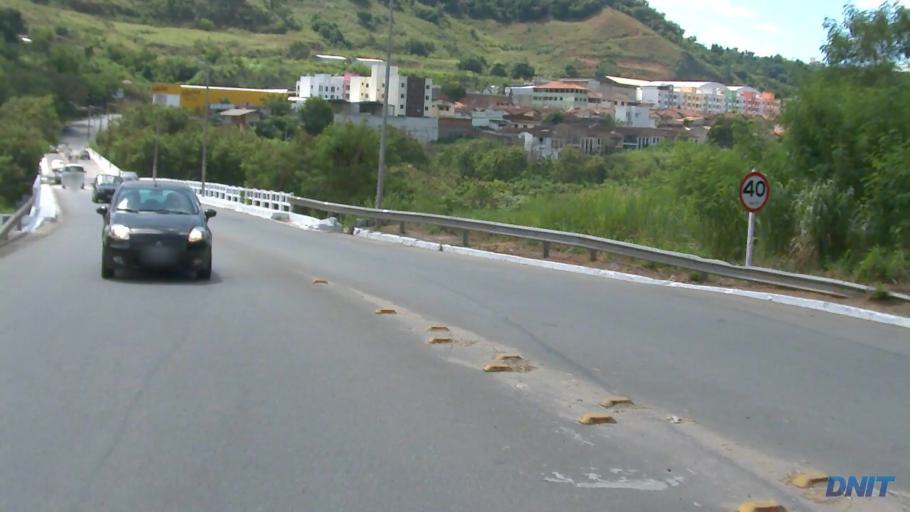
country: BR
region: Minas Gerais
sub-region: Coronel Fabriciano
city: Coronel Fabriciano
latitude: -19.5264
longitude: -42.6405
